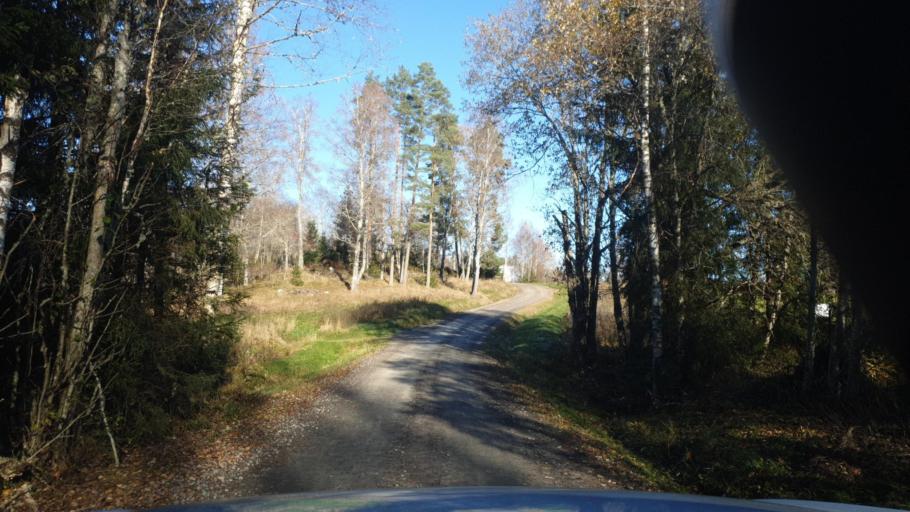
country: SE
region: Vaermland
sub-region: Karlstads Kommun
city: Edsvalla
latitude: 59.4708
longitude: 13.1271
